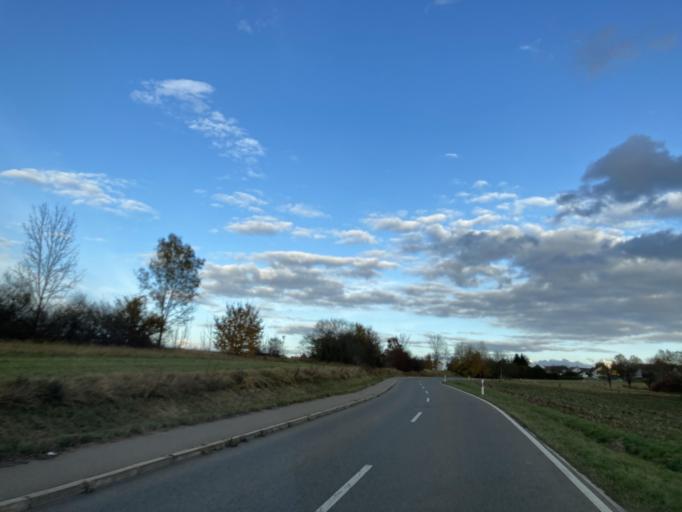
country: DE
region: Baden-Wuerttemberg
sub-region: Tuebingen Region
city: Gomaringen
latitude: 48.4742
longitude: 9.1263
